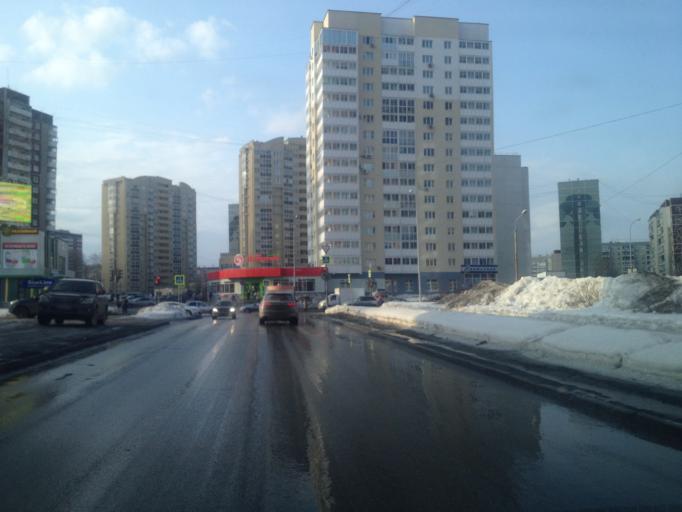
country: RU
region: Sverdlovsk
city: Yekaterinburg
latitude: 56.8532
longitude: 60.5734
